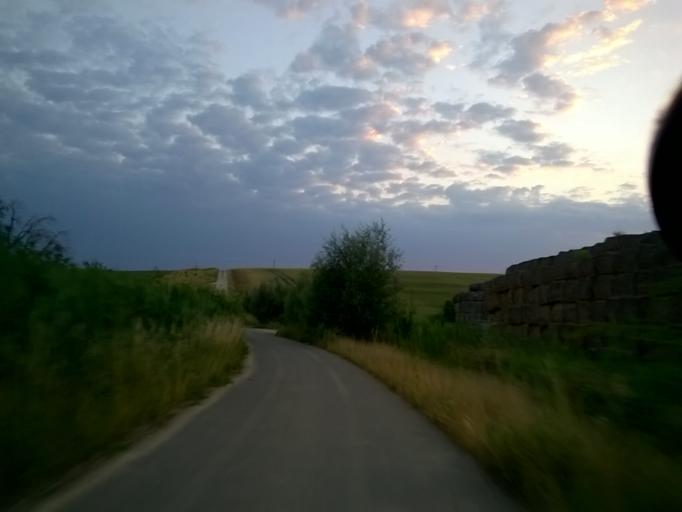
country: SK
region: Trnavsky
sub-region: Okres Senica
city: Senica
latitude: 48.7243
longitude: 17.3363
